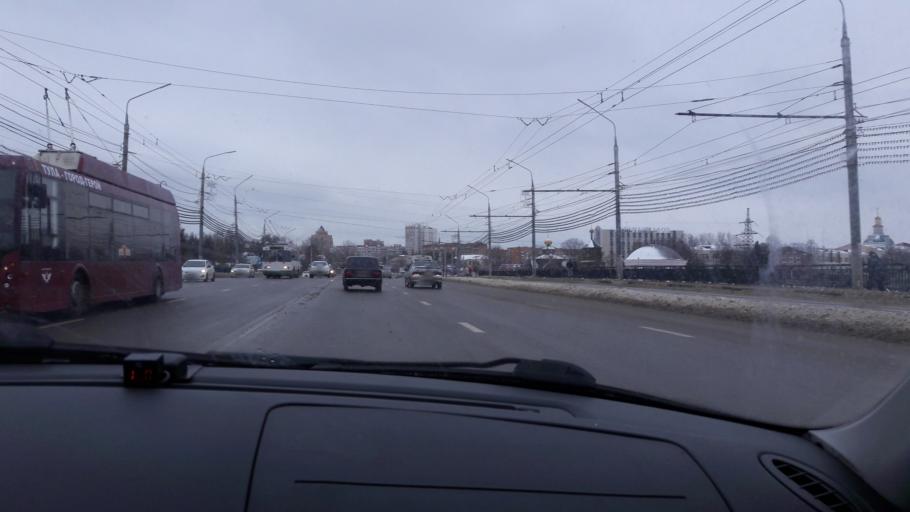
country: RU
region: Tula
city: Tula
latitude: 54.2031
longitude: 37.6172
